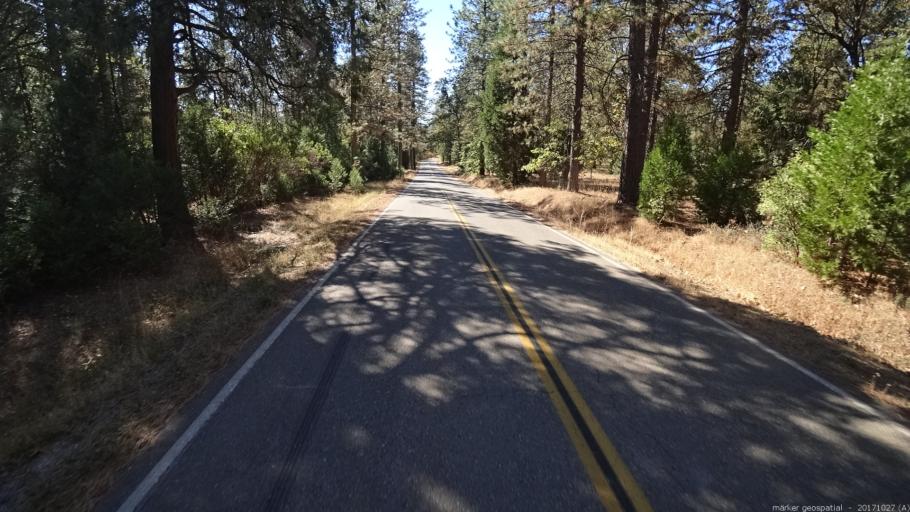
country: US
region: California
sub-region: Shasta County
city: Shingletown
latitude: 40.6962
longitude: -122.0020
